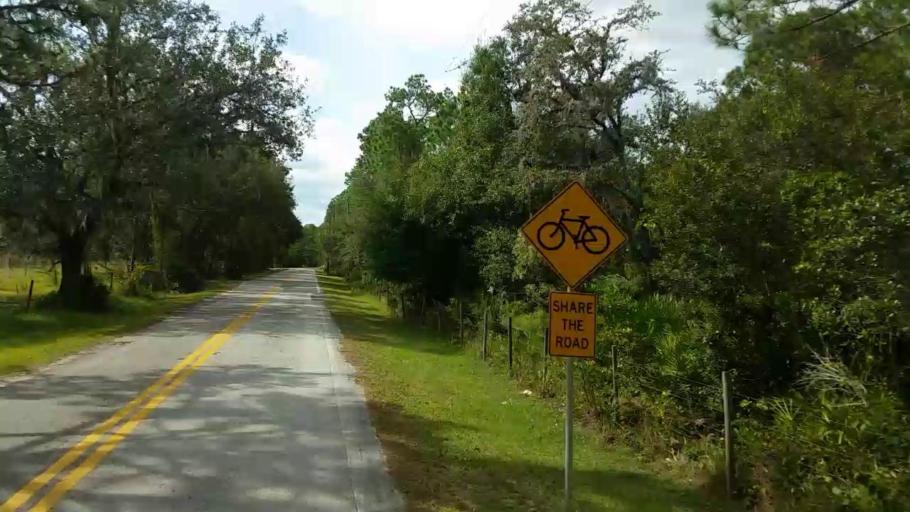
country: US
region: Florida
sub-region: Polk County
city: Polk City
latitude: 28.3257
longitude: -81.8470
